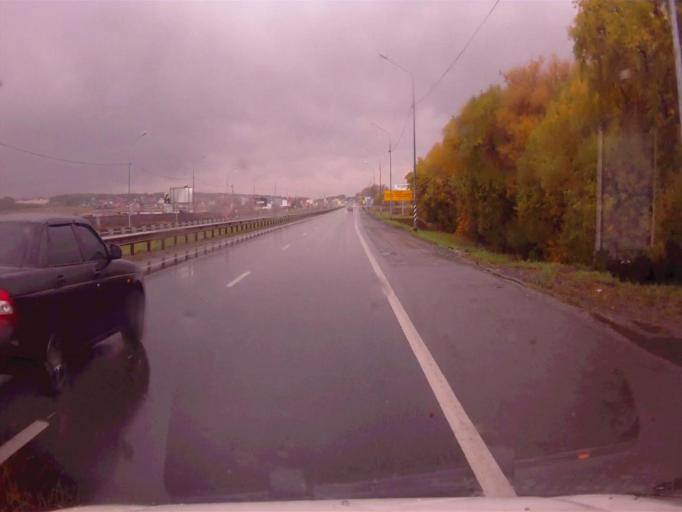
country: RU
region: Chelyabinsk
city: Dolgoderevenskoye
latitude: 55.2706
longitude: 61.3445
